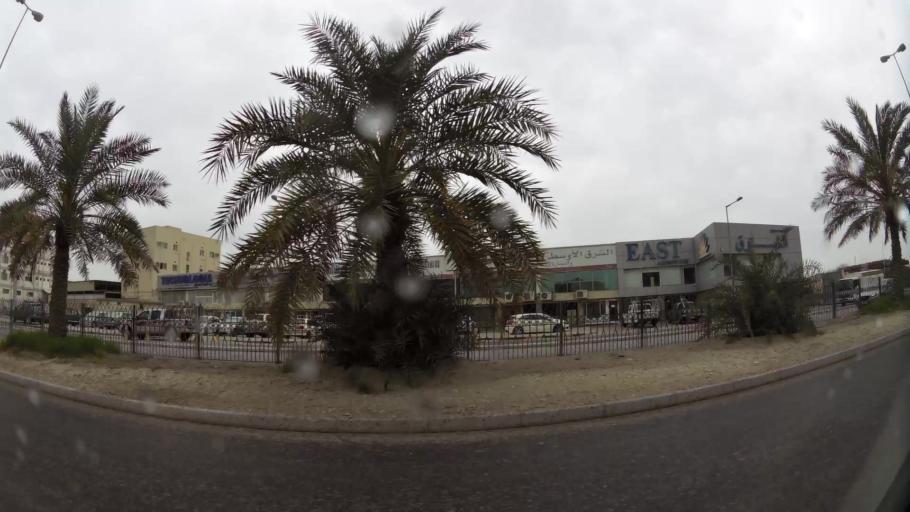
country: BH
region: Northern
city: Madinat `Isa
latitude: 26.1852
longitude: 50.5255
